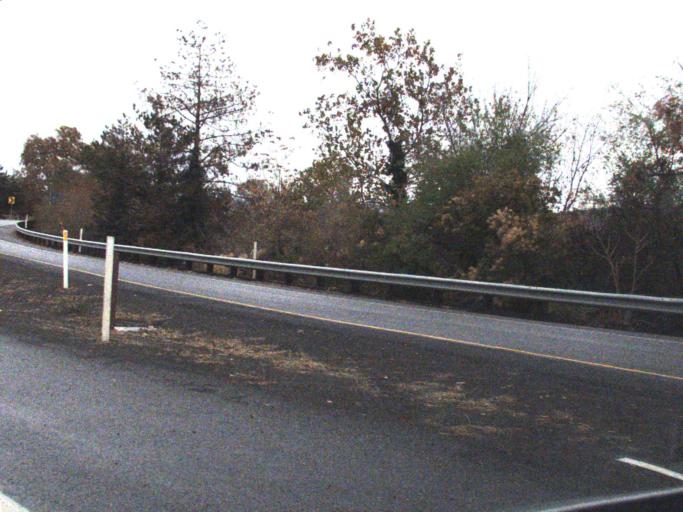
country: US
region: Washington
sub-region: Walla Walla County
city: Walla Walla
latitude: 46.0710
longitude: -118.3474
